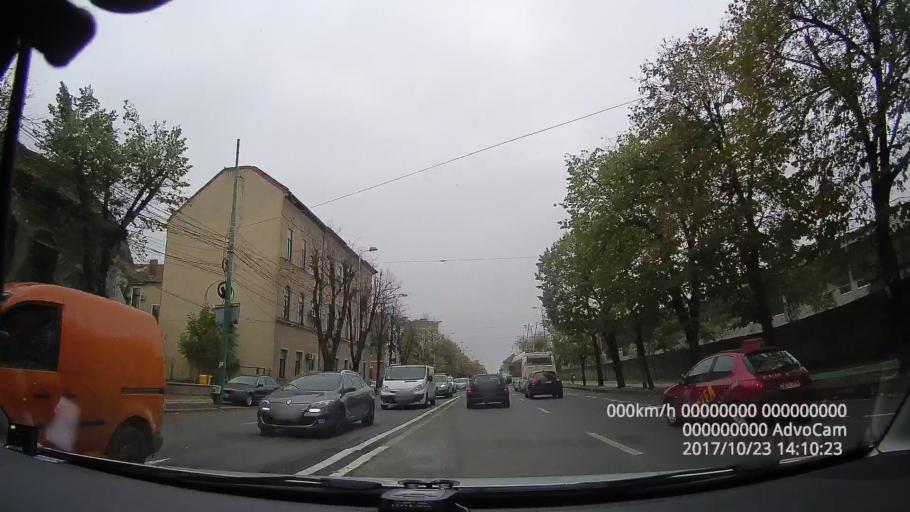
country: RO
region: Timis
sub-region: Oras Recas
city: Izvin
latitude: 45.7986
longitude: 21.4570
